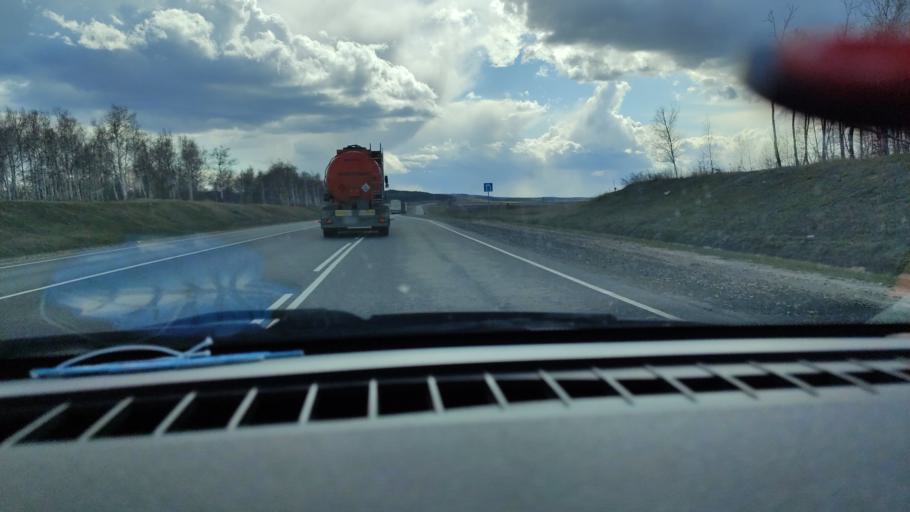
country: RU
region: Saratov
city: Khvalynsk
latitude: 52.5547
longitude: 48.0801
